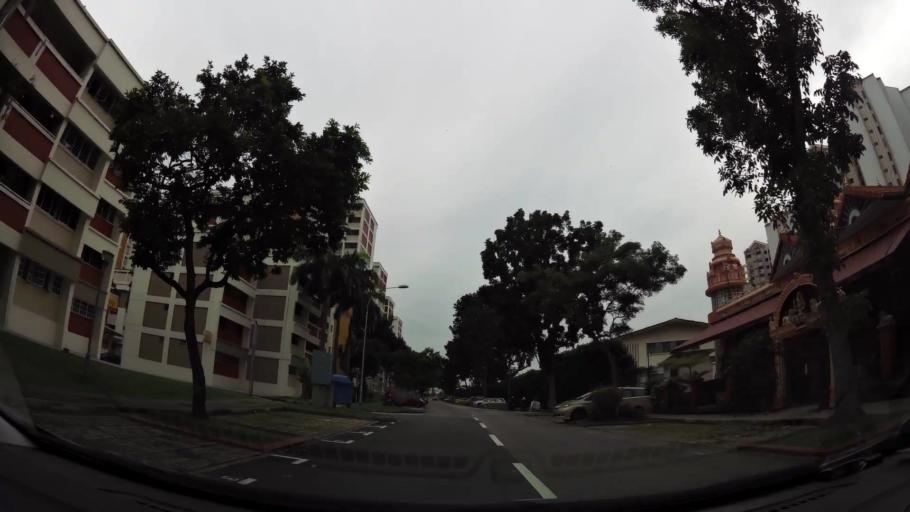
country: SG
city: Singapore
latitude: 1.3685
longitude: 103.8700
